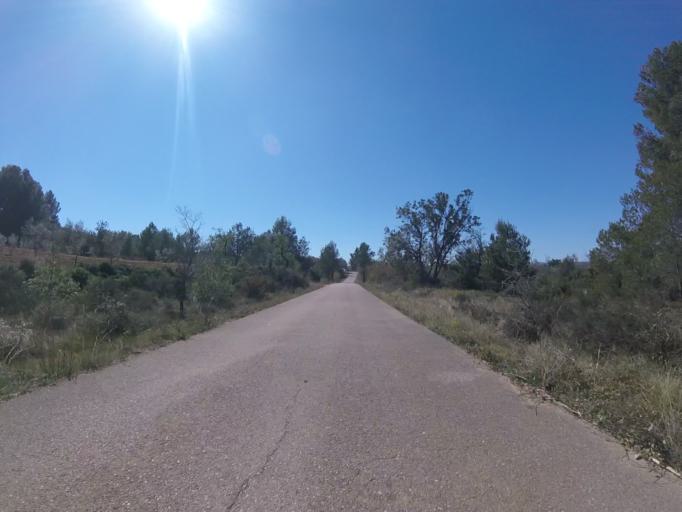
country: ES
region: Valencia
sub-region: Provincia de Castello
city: Cuevas de Vinroma
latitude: 40.3921
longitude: 0.1618
